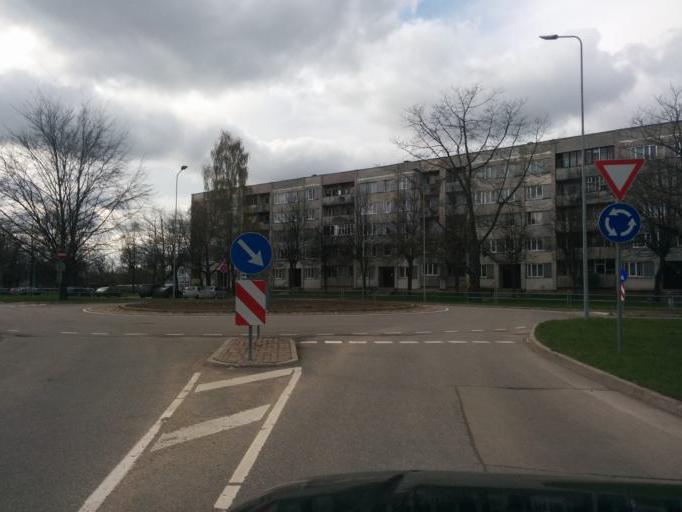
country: LV
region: Ozolnieku
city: Ozolnieki
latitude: 56.6605
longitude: 23.7618
